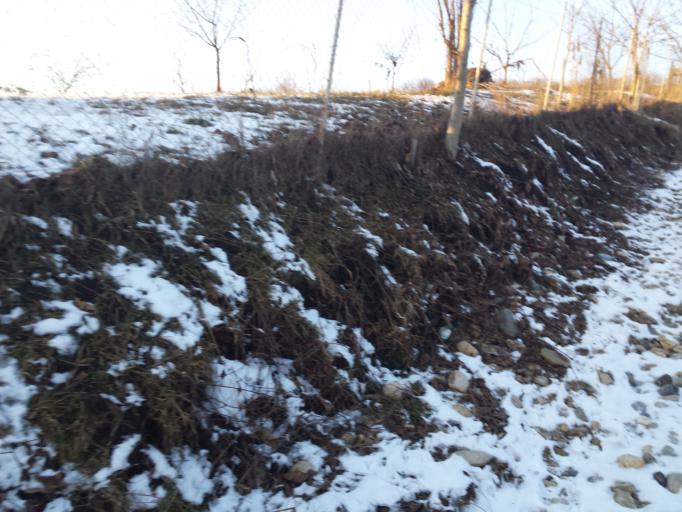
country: RO
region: Cluj
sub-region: Municipiul Cluj-Napoca
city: Cluj-Napoca
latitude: 46.7956
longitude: 23.5842
